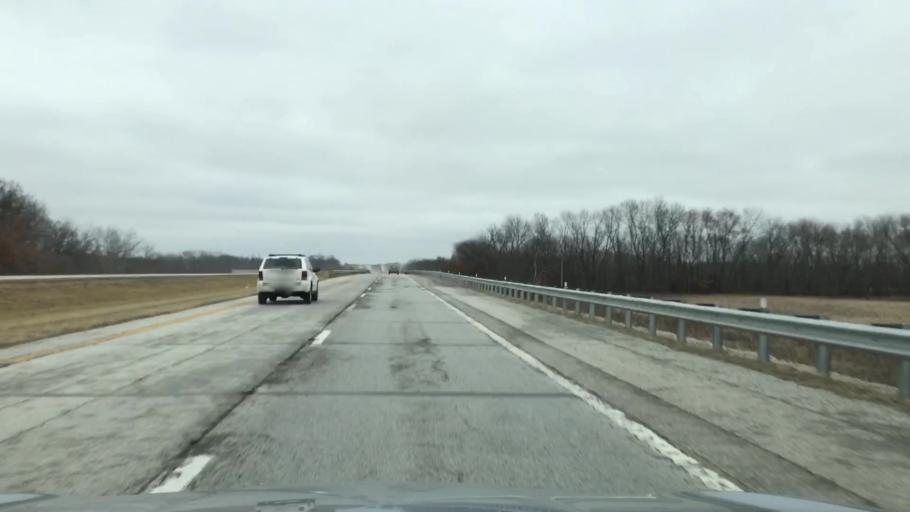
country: US
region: Missouri
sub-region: Linn County
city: Marceline
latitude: 39.7614
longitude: -92.9855
